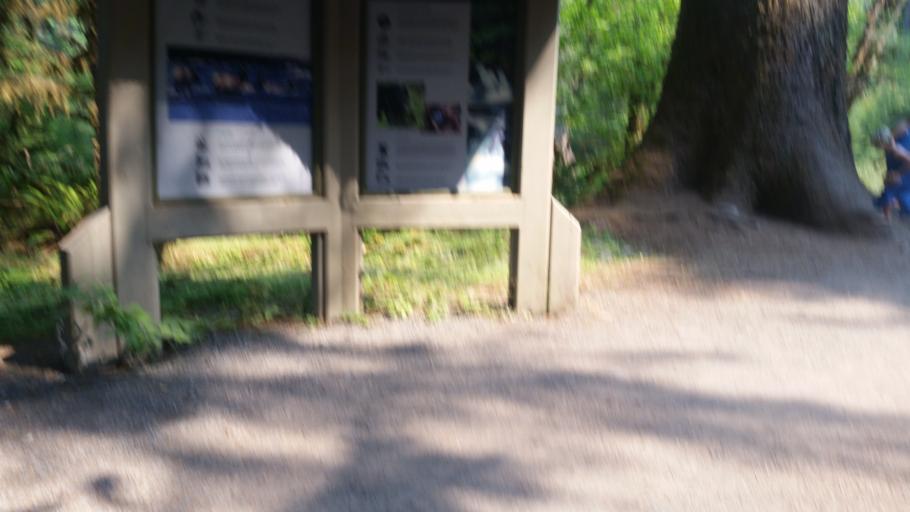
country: US
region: Washington
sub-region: Clallam County
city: Forks
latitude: 47.8605
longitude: -123.9343
